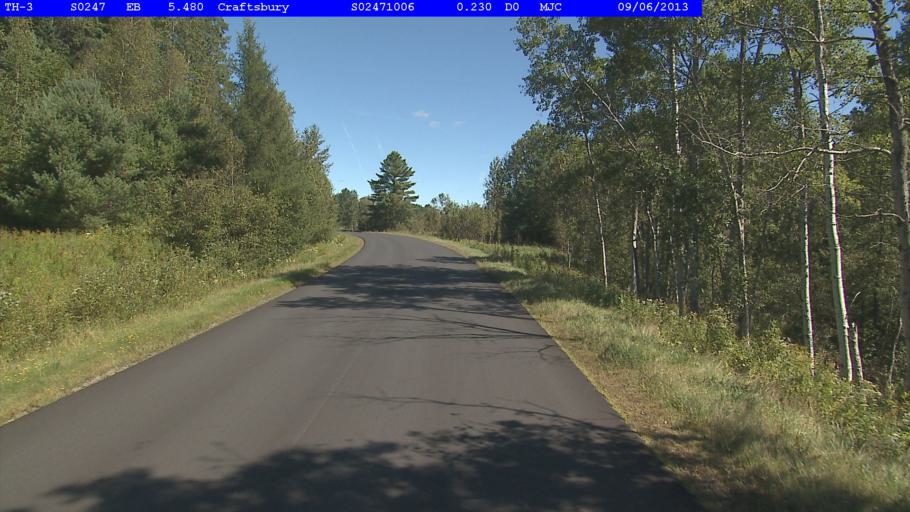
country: US
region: Vermont
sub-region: Caledonia County
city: Hardwick
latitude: 44.6221
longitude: -72.4405
